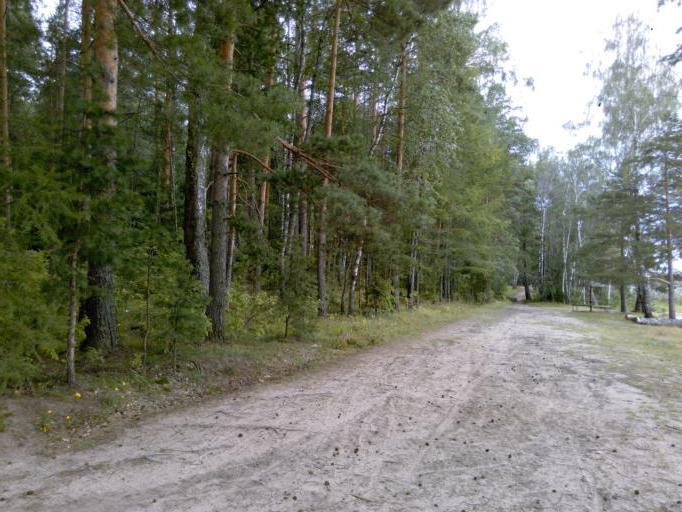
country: RU
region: Tverskaya
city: Konakovo
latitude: 56.6754
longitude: 36.6876
